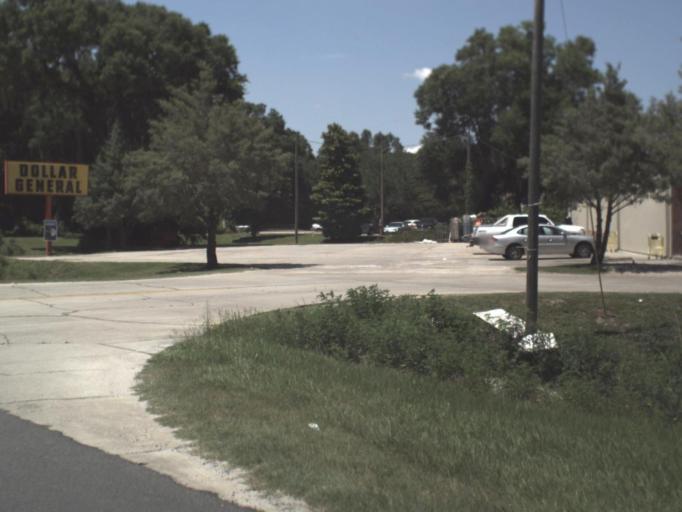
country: US
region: Florida
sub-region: Lafayette County
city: Mayo
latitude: 30.0538
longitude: -83.1808
